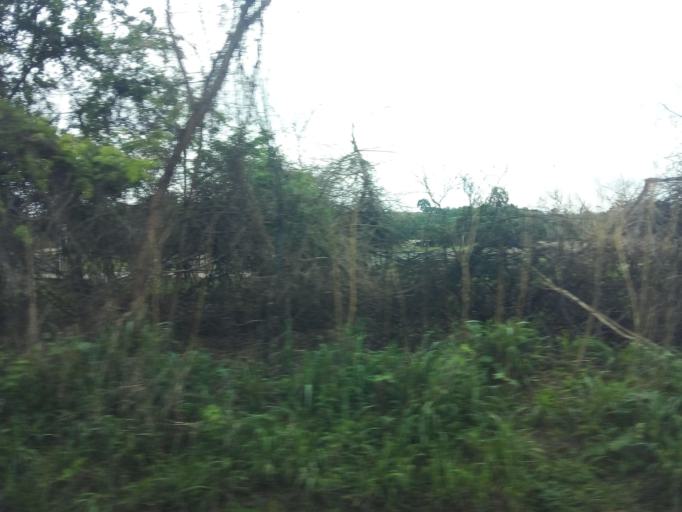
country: BR
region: Minas Gerais
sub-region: Ipatinga
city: Ipatinga
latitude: -19.4754
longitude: -42.4859
